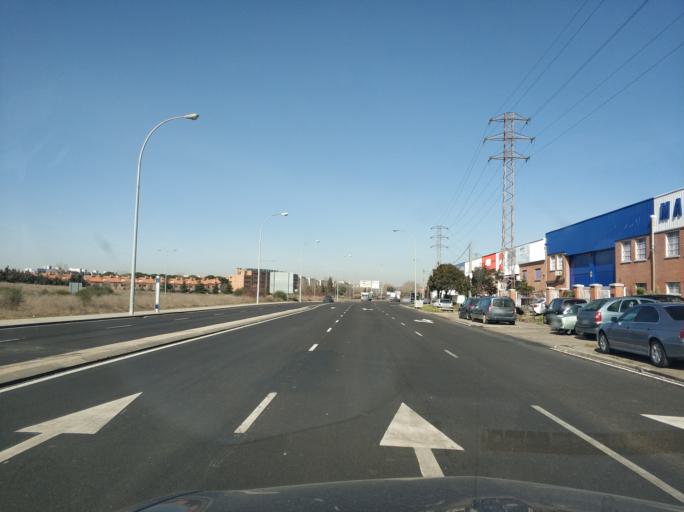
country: ES
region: Castille and Leon
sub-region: Provincia de Valladolid
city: Cisterniga
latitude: 41.6136
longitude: -4.7118
